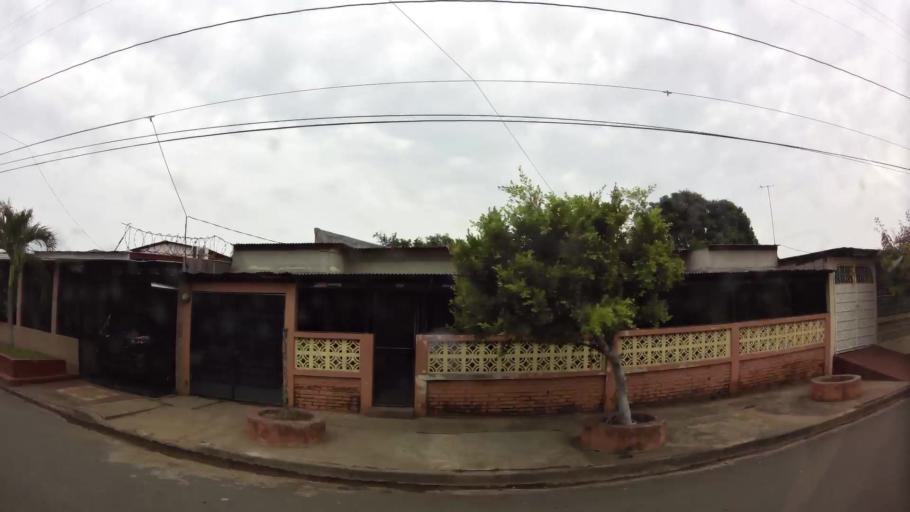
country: NI
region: Granada
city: Granada
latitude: 11.9479
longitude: -85.9506
